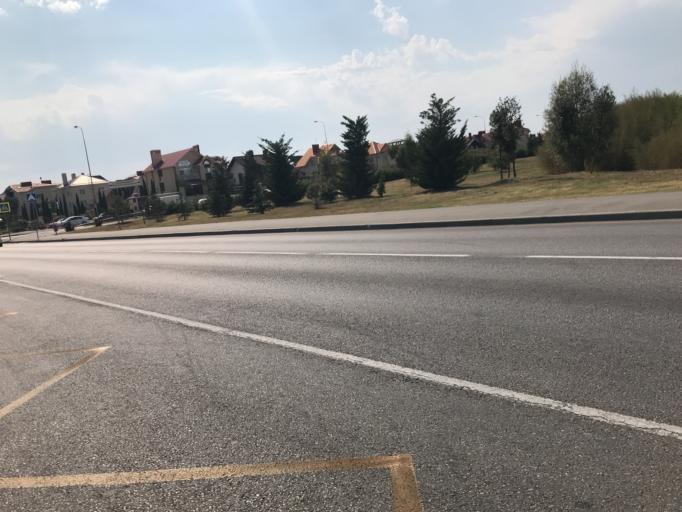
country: RU
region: Krasnodarskiy
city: Adler
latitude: 43.3990
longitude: 39.9760
